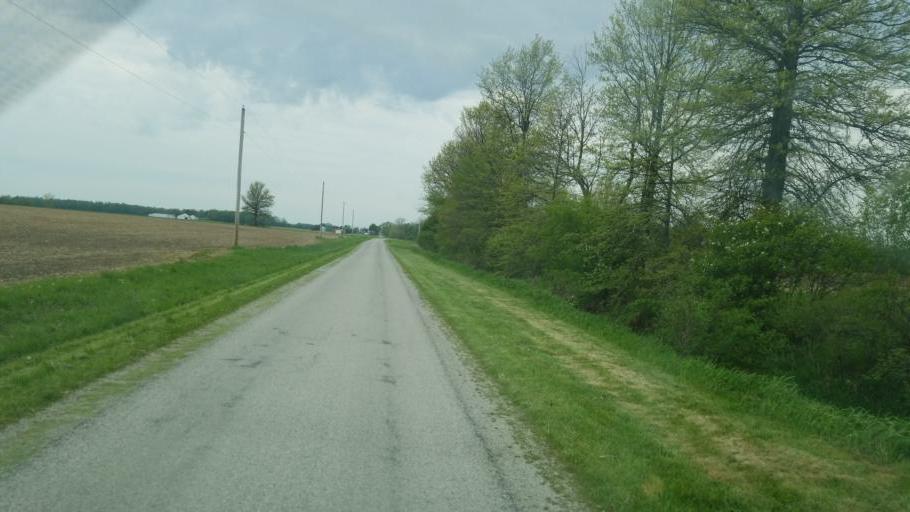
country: US
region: Ohio
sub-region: Huron County
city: Willard
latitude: 41.0080
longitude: -82.8348
